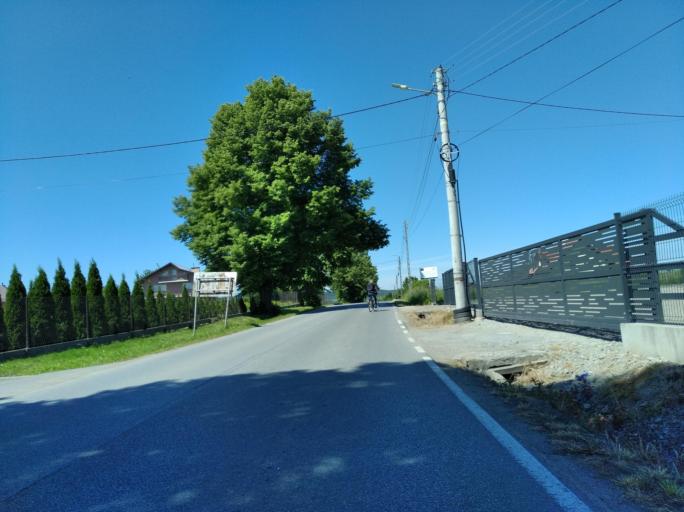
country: PL
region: Subcarpathian Voivodeship
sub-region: Powiat krosnienski
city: Chorkowka
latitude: 49.6592
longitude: 21.6941
